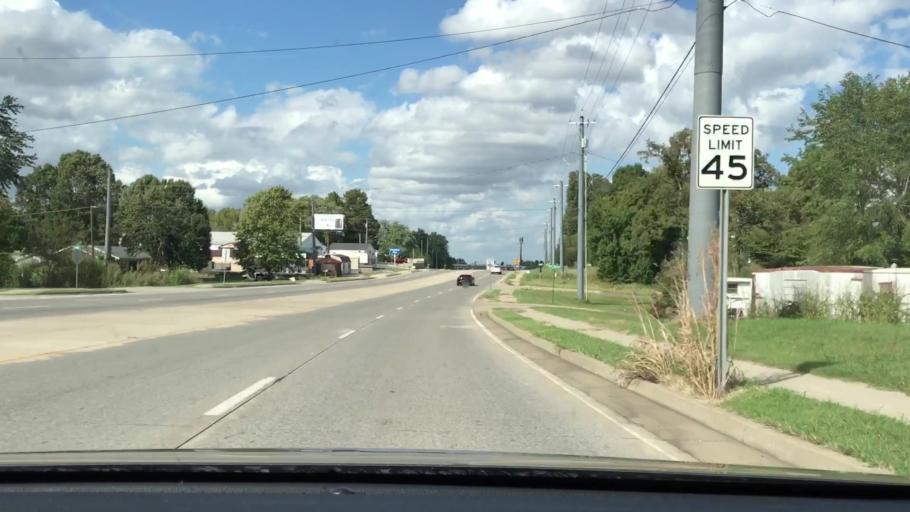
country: US
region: Kentucky
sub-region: Graves County
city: Mayfield
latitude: 36.7621
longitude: -88.6426
